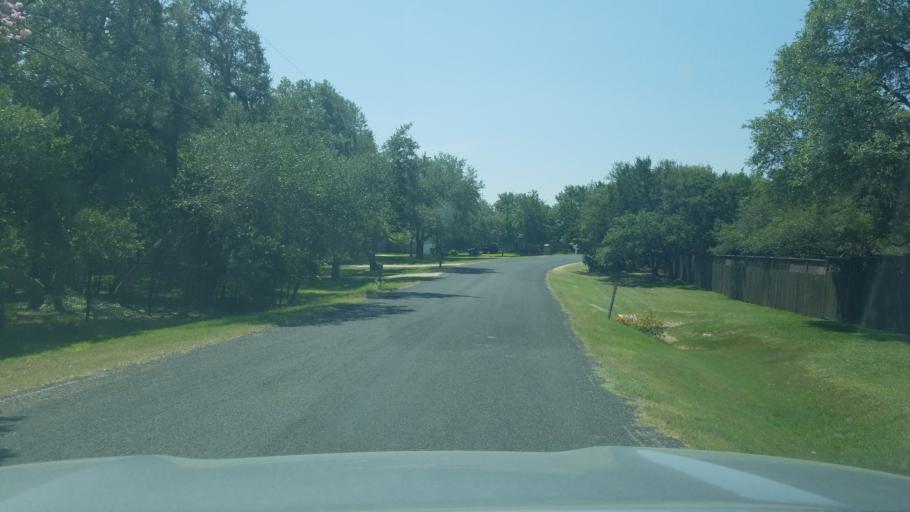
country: US
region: Texas
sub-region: Bexar County
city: Timberwood Park
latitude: 29.7012
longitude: -98.4861
